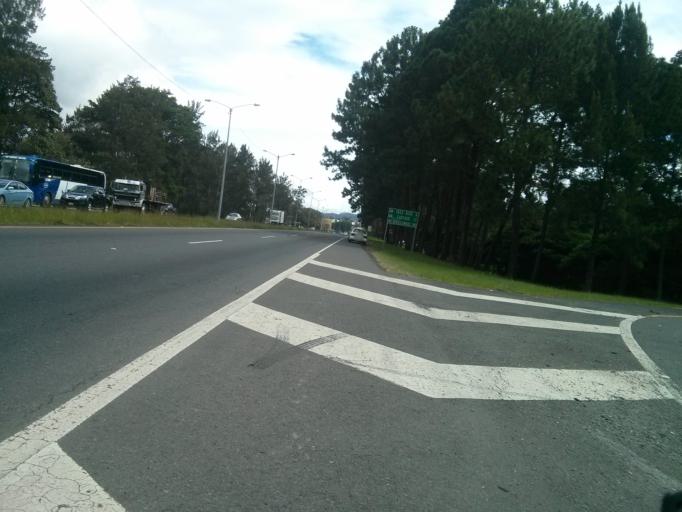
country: CR
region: San Jose
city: Curridabat
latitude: 9.9125
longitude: -84.0268
